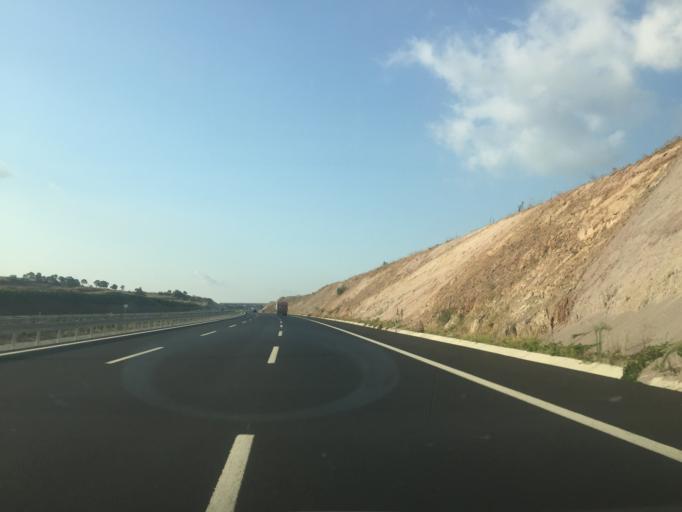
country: TR
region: Balikesir
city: Ertugrul
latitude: 39.6030
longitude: 27.7031
